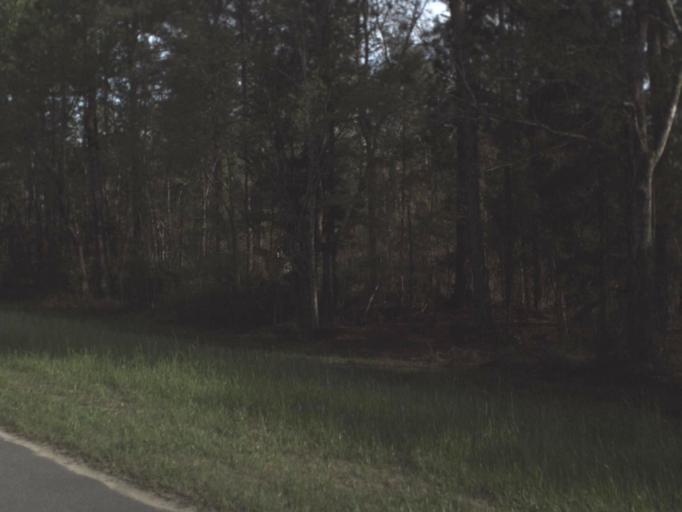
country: US
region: Florida
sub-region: Holmes County
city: Bonifay
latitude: 30.7910
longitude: -85.7076
